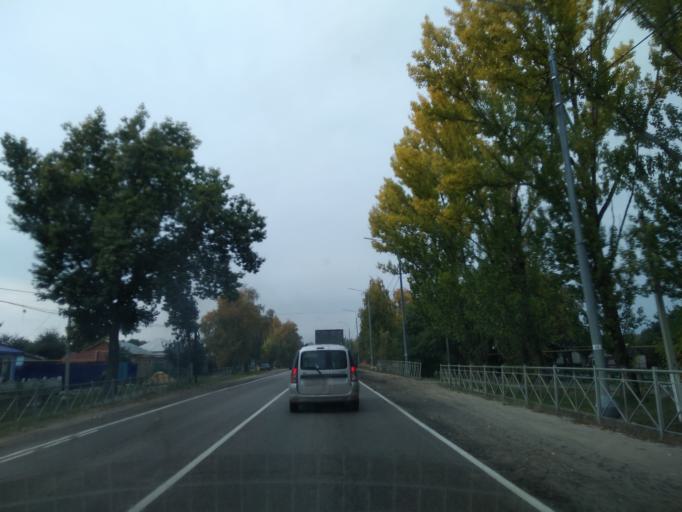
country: RU
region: Lipetsk
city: Zadonsk
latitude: 52.4145
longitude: 38.8663
